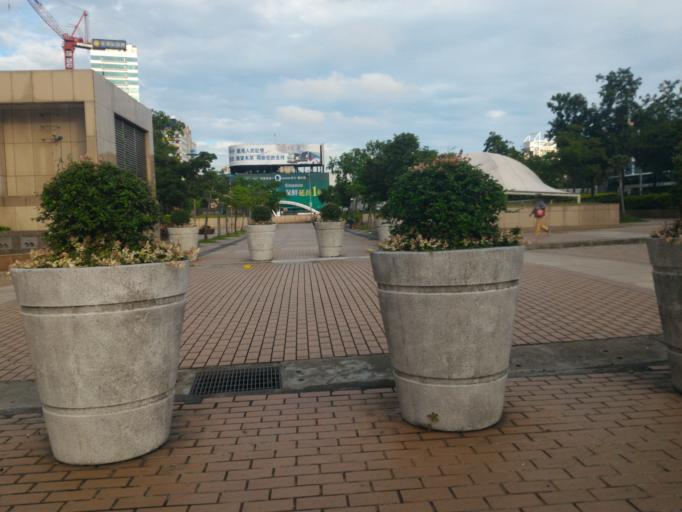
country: TW
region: Taipei
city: Taipei
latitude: 25.0469
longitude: 121.5161
